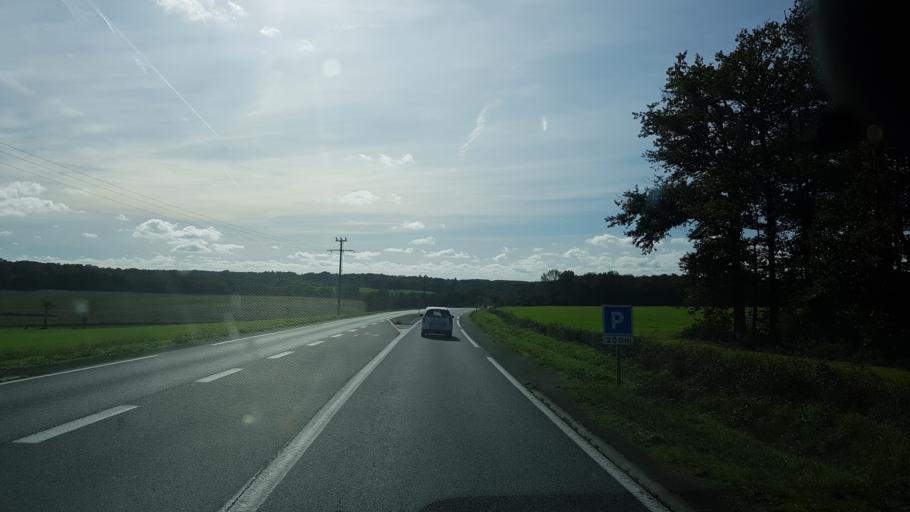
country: FR
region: Poitou-Charentes
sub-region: Departement de la Charente
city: Loubert
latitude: 45.9685
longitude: 0.5885
